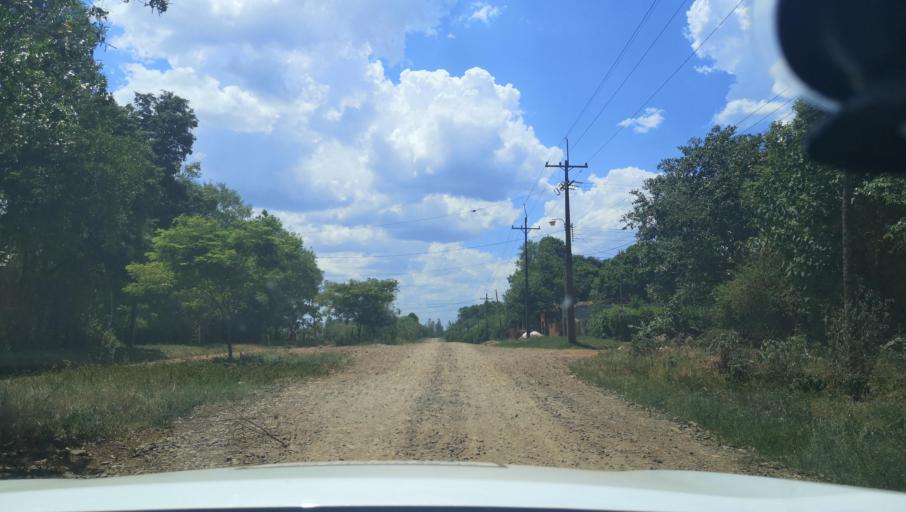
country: PY
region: Itapua
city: Carmen del Parana
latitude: -27.1655
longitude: -56.2491
